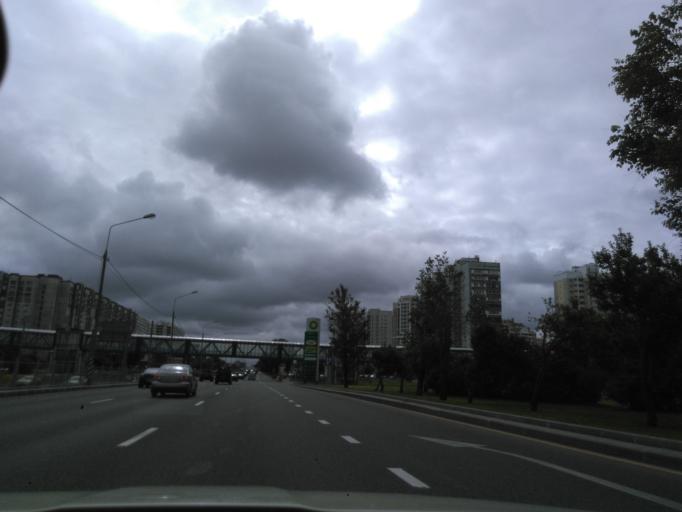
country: RU
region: Moskovskaya
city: Bol'shaya Setun'
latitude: 55.7430
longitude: 37.4258
